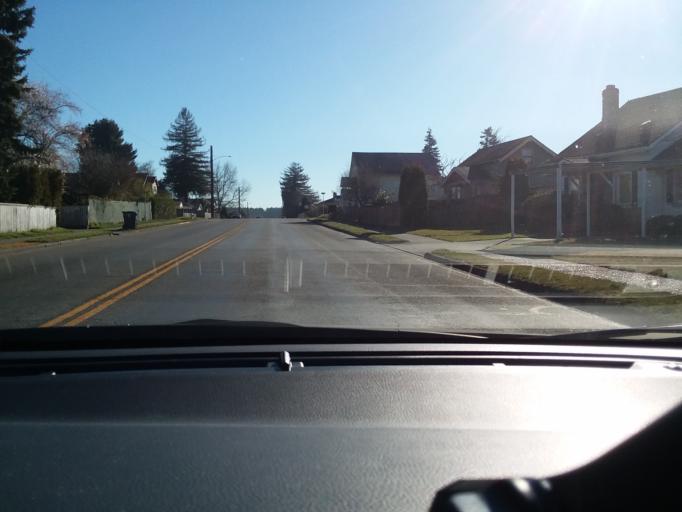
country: US
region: Washington
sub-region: Pierce County
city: Midland
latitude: 47.2063
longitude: -122.4182
